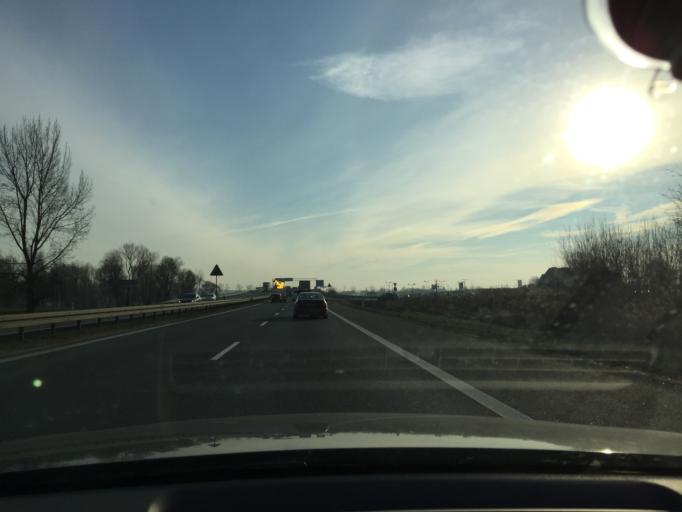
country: PL
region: Lesser Poland Voivodeship
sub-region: Powiat krakowski
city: Balice
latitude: 50.0750
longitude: 19.8095
